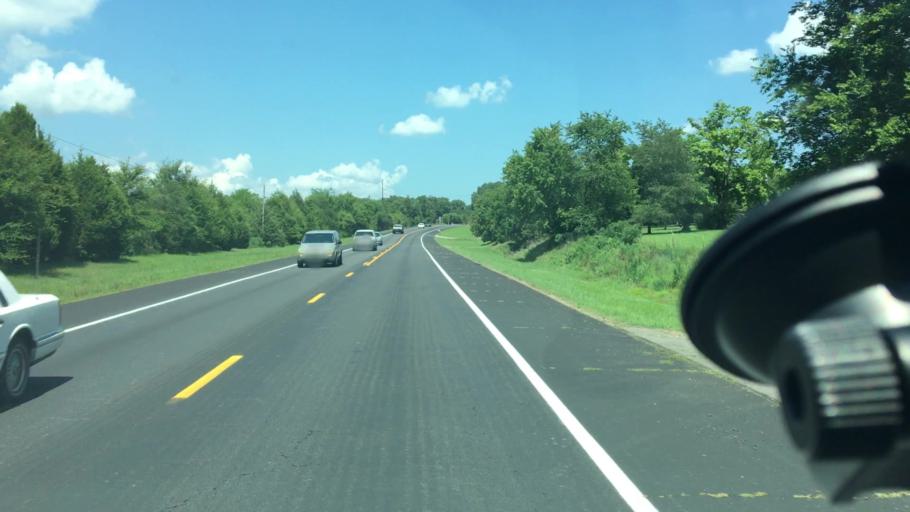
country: US
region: Arkansas
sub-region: Sebastian County
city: Lavaca
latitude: 35.2983
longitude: -94.1540
